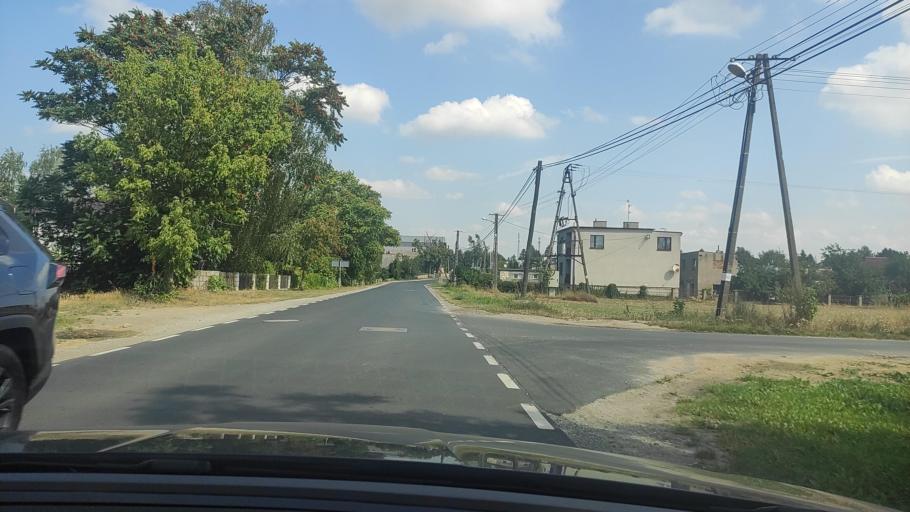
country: PL
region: Greater Poland Voivodeship
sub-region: Powiat poznanski
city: Kostrzyn
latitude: 52.4602
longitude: 17.1676
